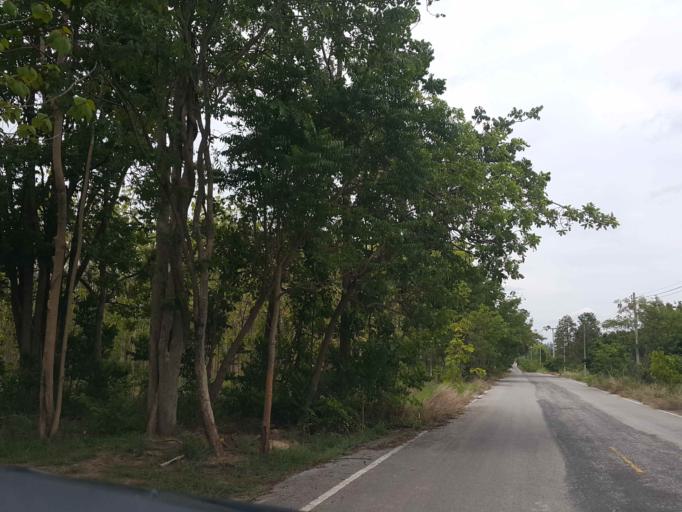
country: TH
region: Chiang Mai
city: Doi Lo
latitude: 18.5049
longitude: 98.7629
